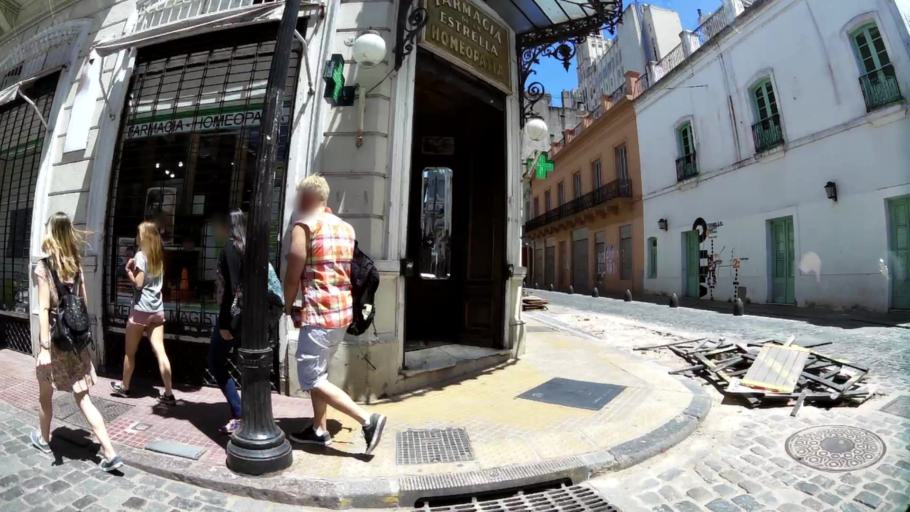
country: AR
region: Buenos Aires F.D.
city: Buenos Aires
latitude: -34.6102
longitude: -58.3721
